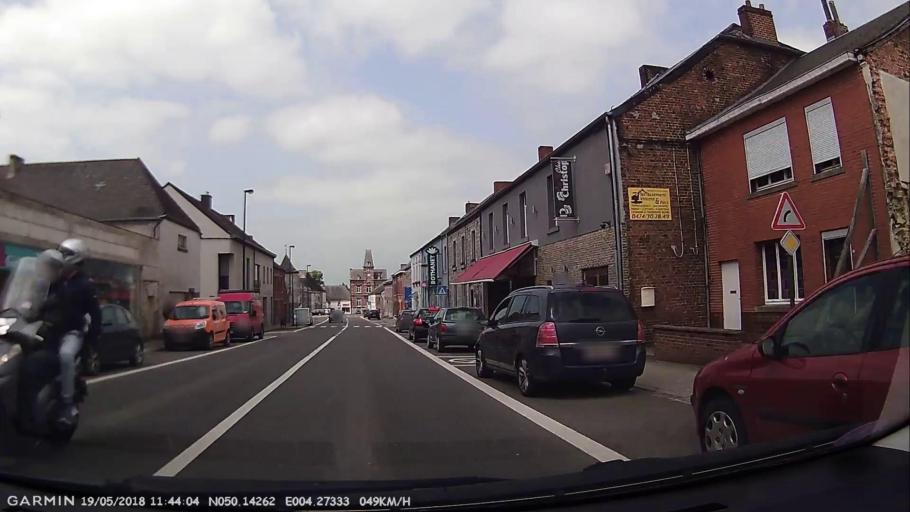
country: BE
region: Wallonia
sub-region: Province du Hainaut
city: Froidchapelle
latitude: 50.1427
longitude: 4.2730
